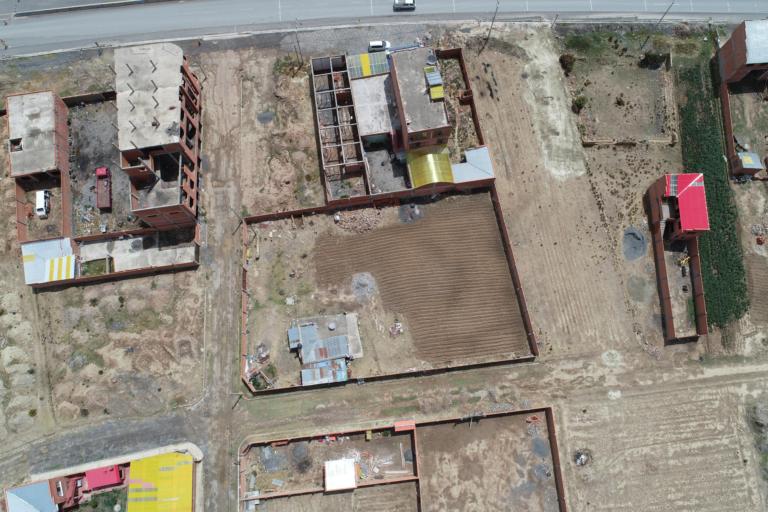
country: BO
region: La Paz
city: Achacachi
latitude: -16.0550
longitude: -68.6811
